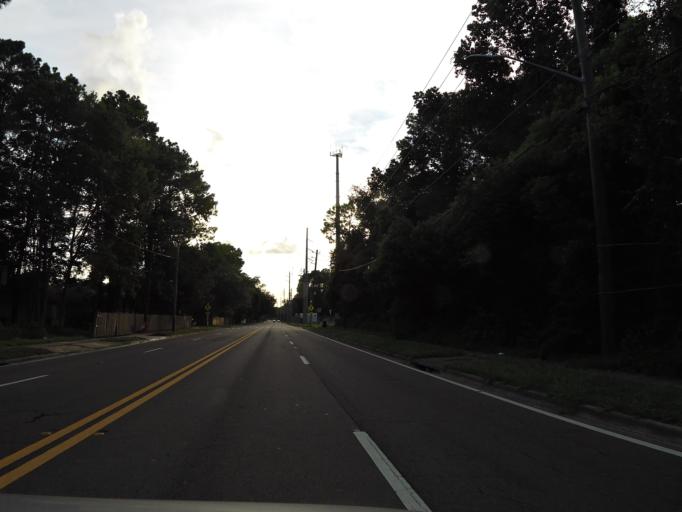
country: US
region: Florida
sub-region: Duval County
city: Jacksonville
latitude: 30.4043
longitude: -81.7124
